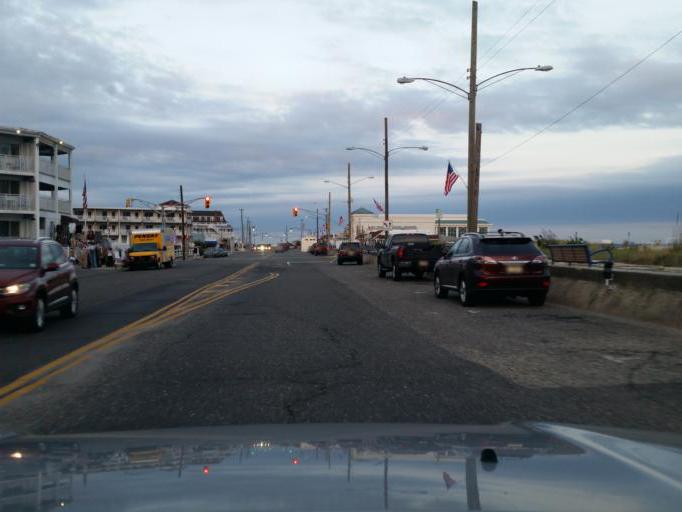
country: US
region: New Jersey
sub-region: Cape May County
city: Cape May
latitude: 38.9304
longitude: -74.9205
